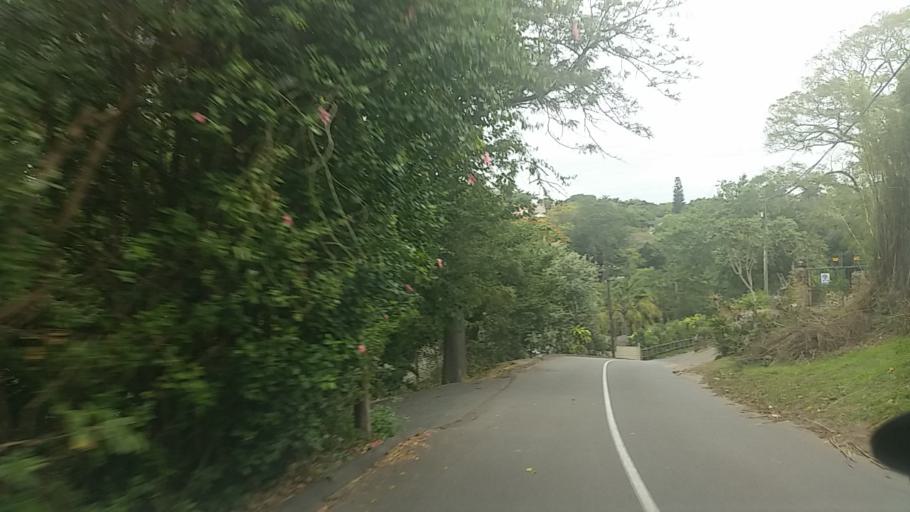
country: ZA
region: KwaZulu-Natal
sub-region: eThekwini Metropolitan Municipality
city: Berea
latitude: -29.8404
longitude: 30.9349
